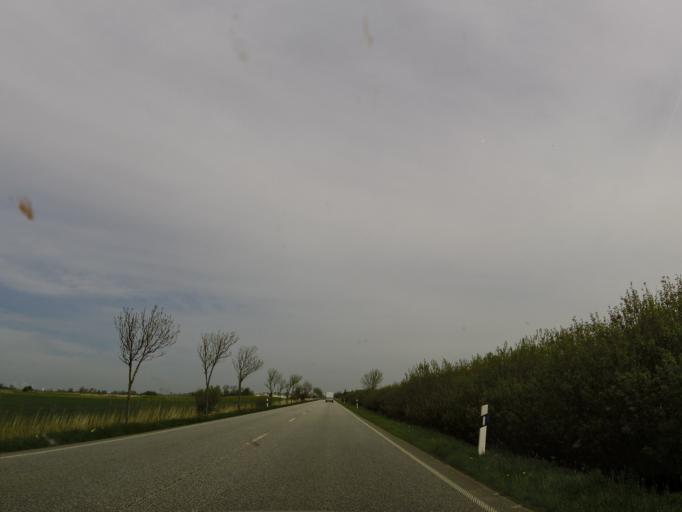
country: DE
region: Schleswig-Holstein
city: Koldenbuttel
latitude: 54.4064
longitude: 9.0357
